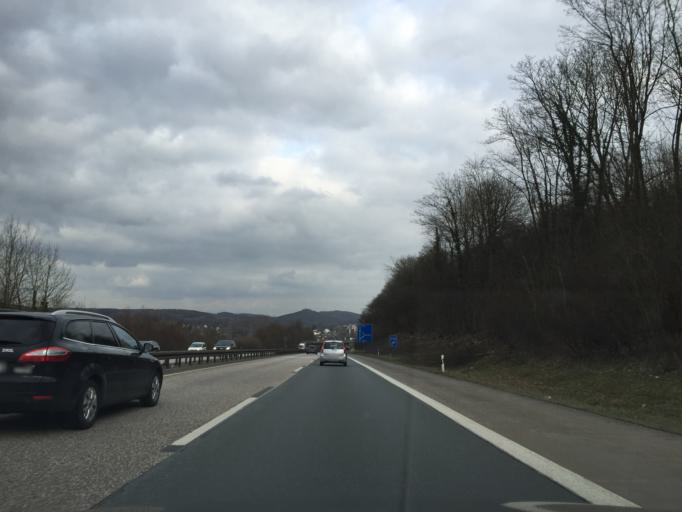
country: DE
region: North Rhine-Westphalia
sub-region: Regierungsbezirk Arnsberg
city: Hagen
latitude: 51.3686
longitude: 7.5330
